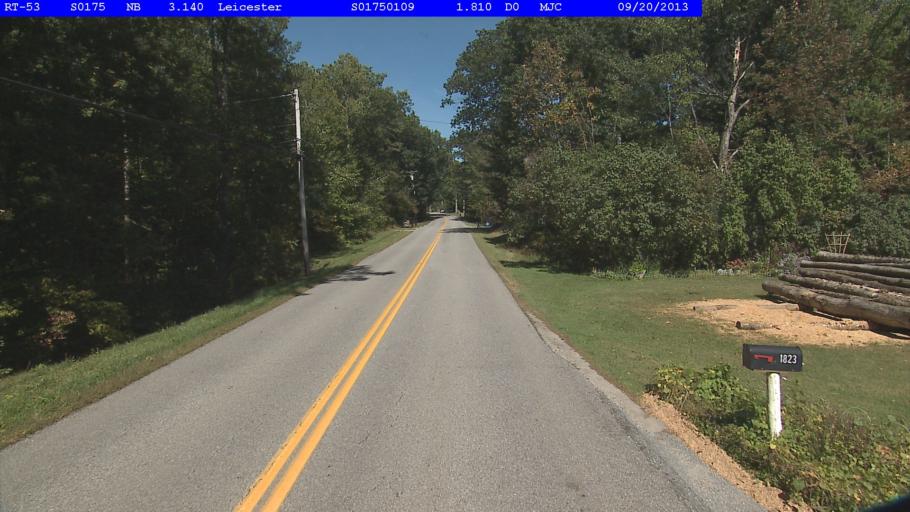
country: US
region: Vermont
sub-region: Rutland County
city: Brandon
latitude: 43.8689
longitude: -73.0651
